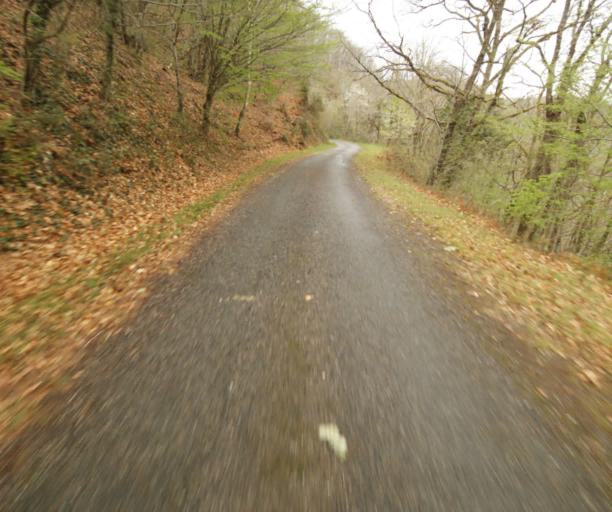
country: FR
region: Limousin
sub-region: Departement de la Correze
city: Saint-Privat
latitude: 45.2073
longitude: 2.0324
